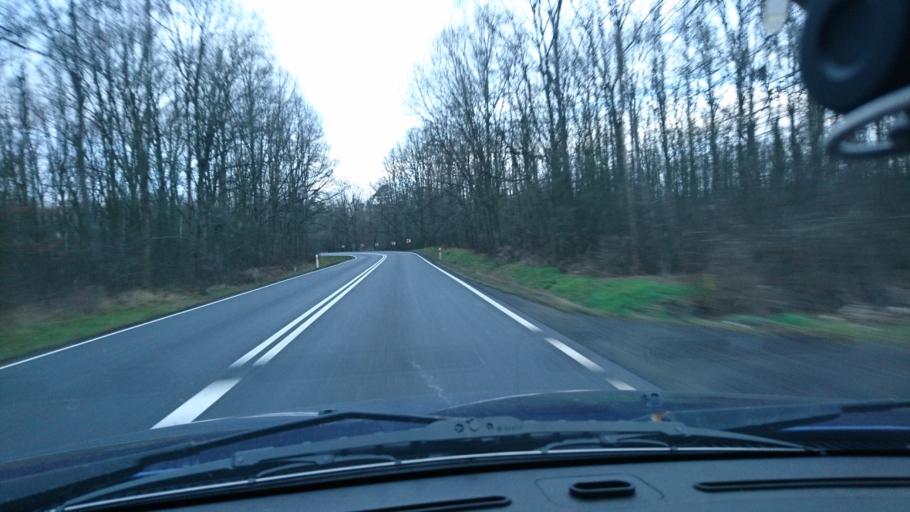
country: PL
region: Opole Voivodeship
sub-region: Powiat kluczborski
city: Byczyna
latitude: 51.1450
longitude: 18.1912
